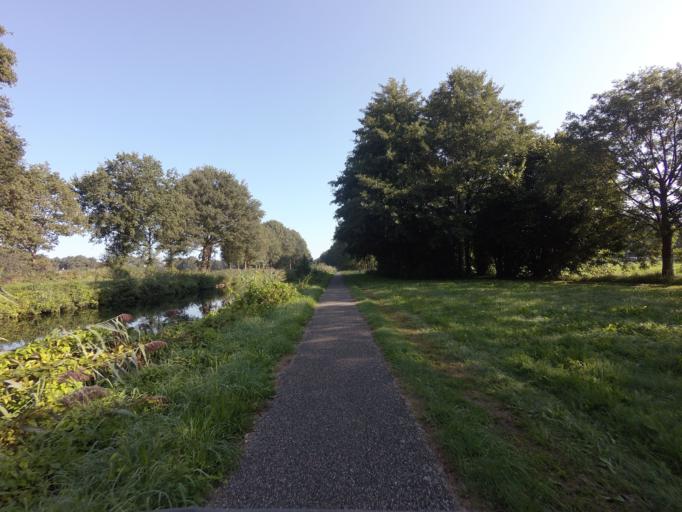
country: NL
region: Overijssel
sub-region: Gemeente Raalte
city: Raalte
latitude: 52.3394
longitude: 6.2708
